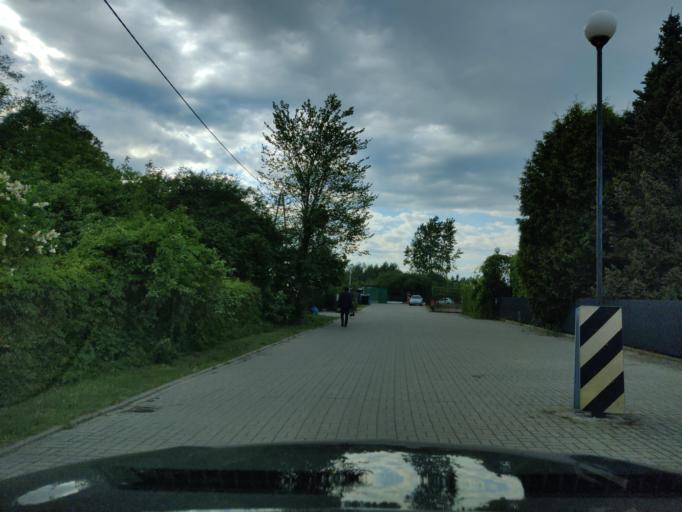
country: PL
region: Masovian Voivodeship
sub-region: Warszawa
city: Kabaty
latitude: 52.1281
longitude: 21.0909
